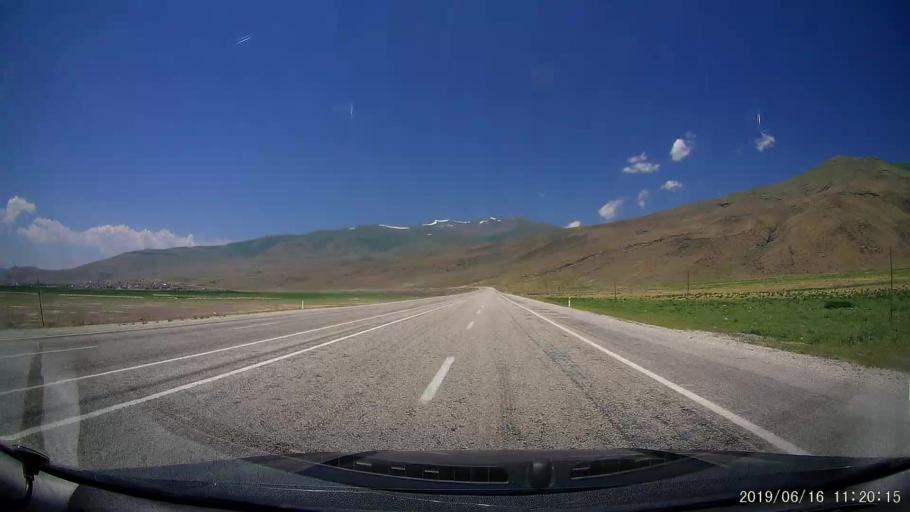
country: TR
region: Agri
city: Dogubayazit
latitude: 39.6980
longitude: 44.0949
